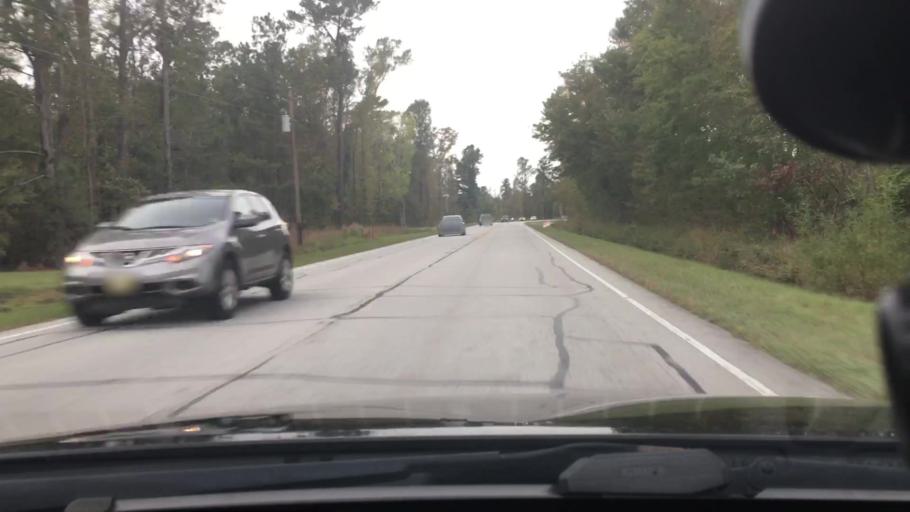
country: US
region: North Carolina
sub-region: Craven County
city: Vanceboro
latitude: 35.3268
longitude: -77.1691
